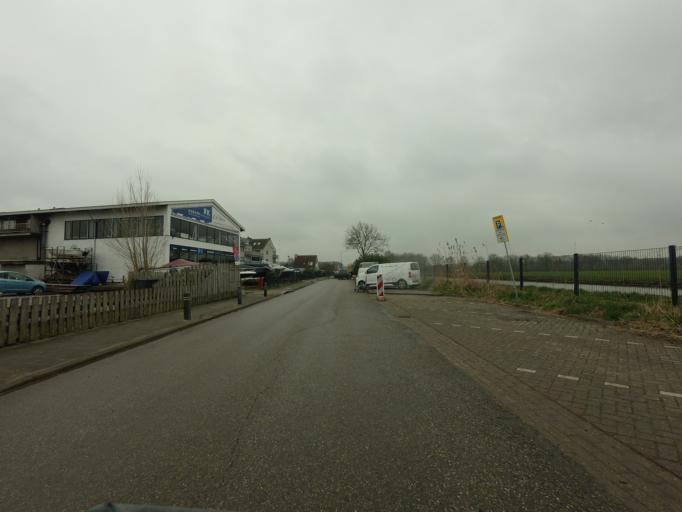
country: NL
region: Utrecht
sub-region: Stichtse Vecht
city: Breukelen
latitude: 52.1800
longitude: 5.0200
